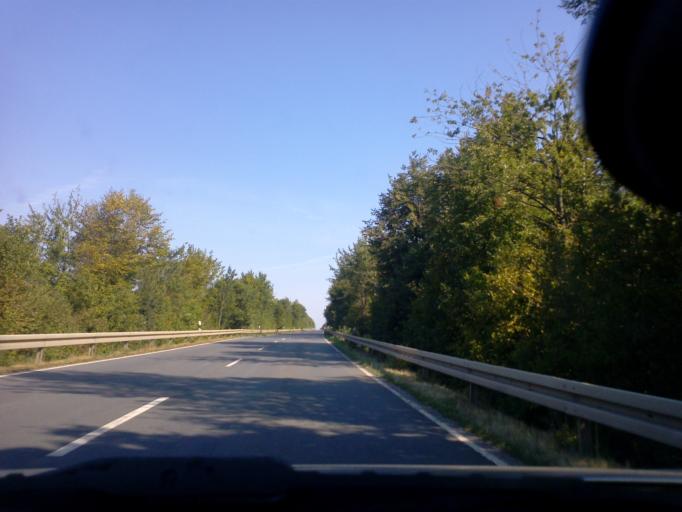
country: DE
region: Baden-Wuerttemberg
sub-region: Regierungsbezirk Stuttgart
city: Gemmingen
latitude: 49.1300
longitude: 9.0014
